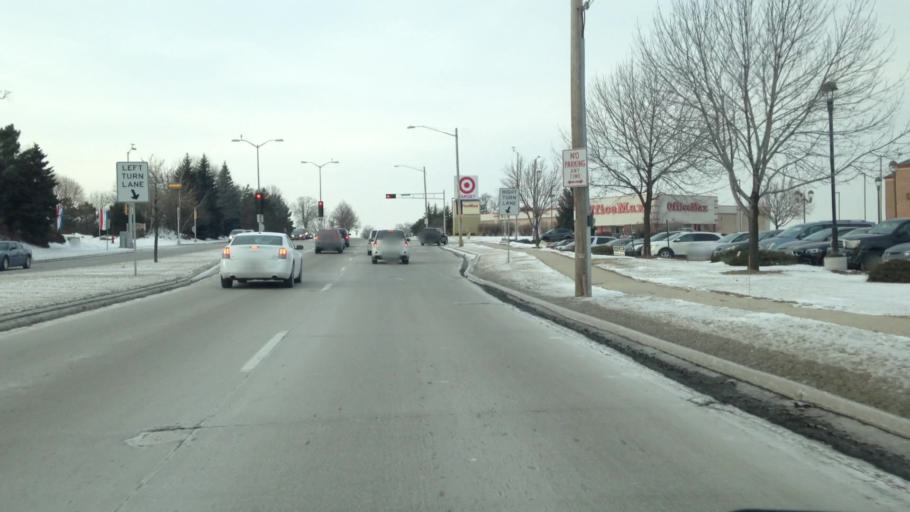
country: US
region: Wisconsin
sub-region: Waukesha County
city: Menomonee Falls
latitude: 43.1867
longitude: -88.1278
